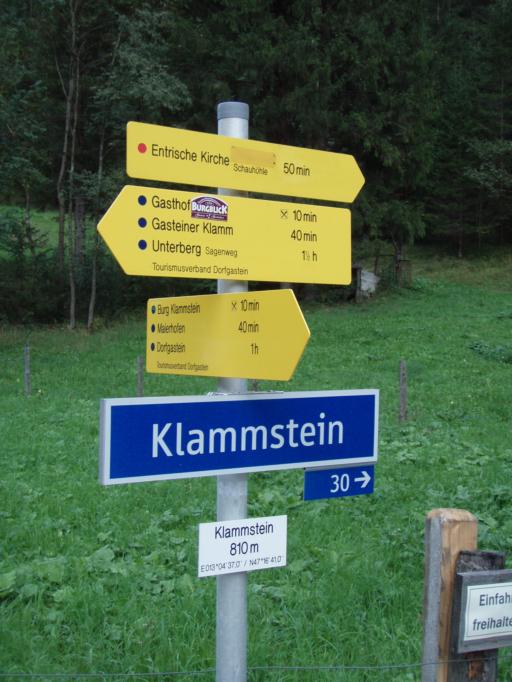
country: AT
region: Salzburg
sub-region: Politischer Bezirk Zell am See
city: Lend
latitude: 47.2781
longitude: 13.0769
